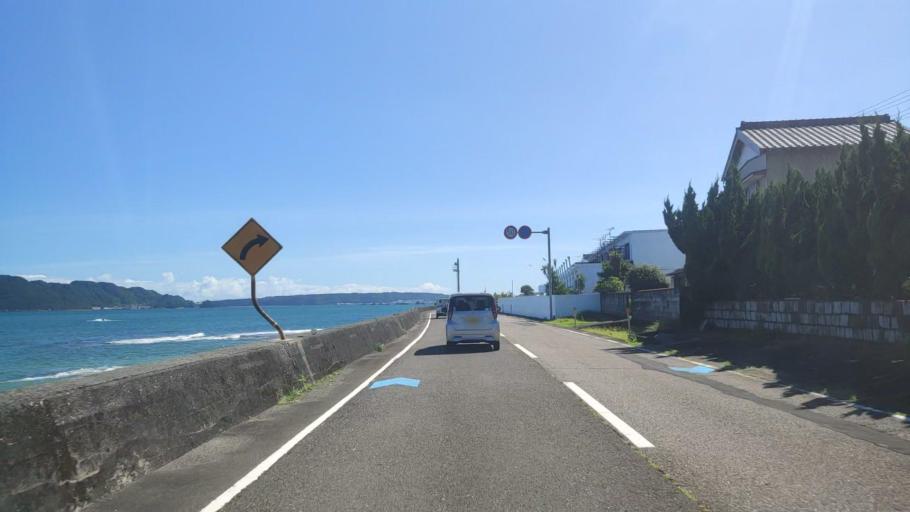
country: JP
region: Wakayama
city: Shingu
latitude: 33.5030
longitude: 135.8120
